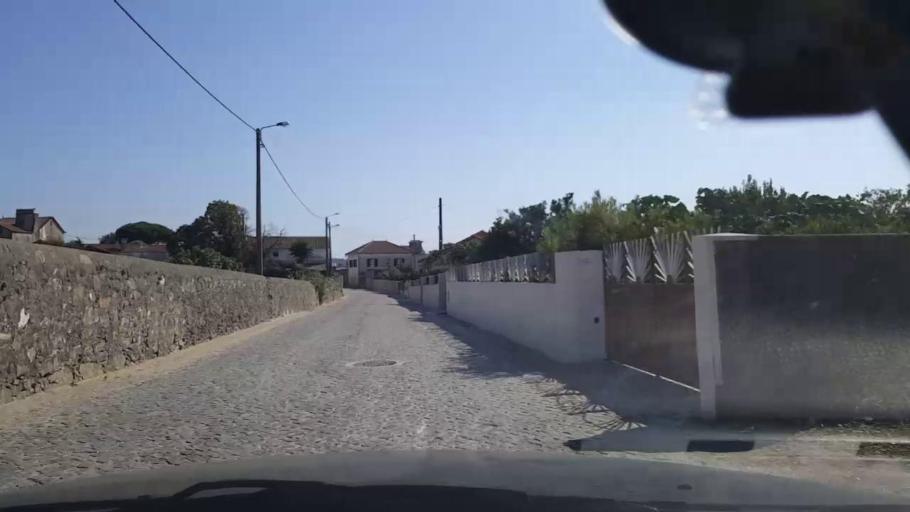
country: PT
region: Porto
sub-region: Povoa de Varzim
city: Pedroso
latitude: 41.4023
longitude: -8.6865
